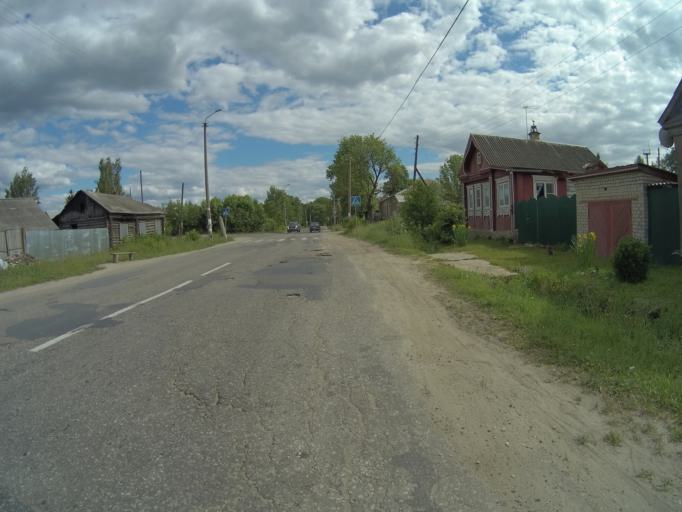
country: RU
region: Vladimir
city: Sudogda
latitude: 55.9509
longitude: 40.8484
